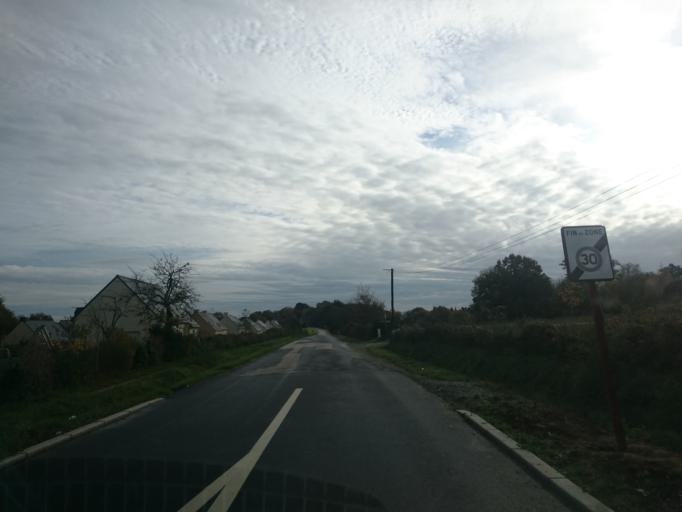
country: FR
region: Brittany
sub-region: Departement d'Ille-et-Vilaine
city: Bourg-des-Comptes
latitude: 47.9279
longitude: -1.7326
